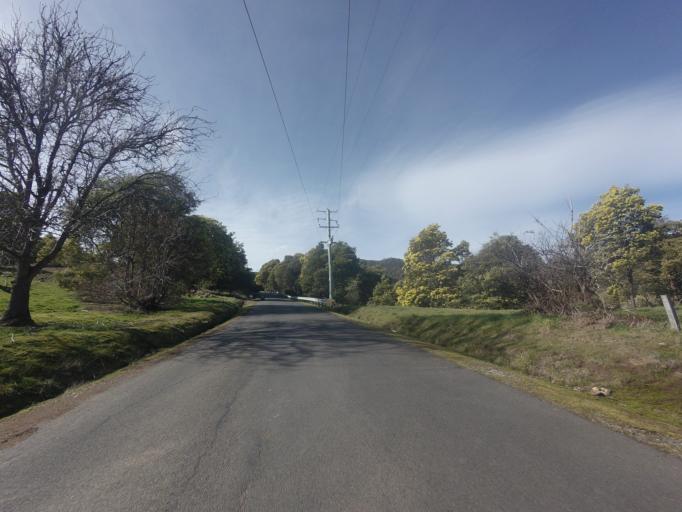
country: AU
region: Tasmania
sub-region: Huon Valley
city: Cygnet
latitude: -43.1742
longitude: 147.1608
